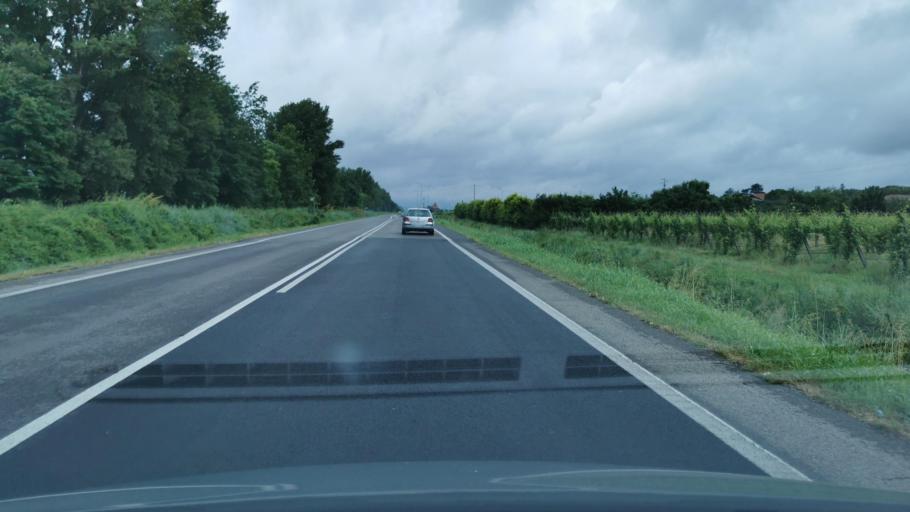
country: IT
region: Emilia-Romagna
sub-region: Provincia di Ravenna
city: Granarolo
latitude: 44.3460
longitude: 11.9239
